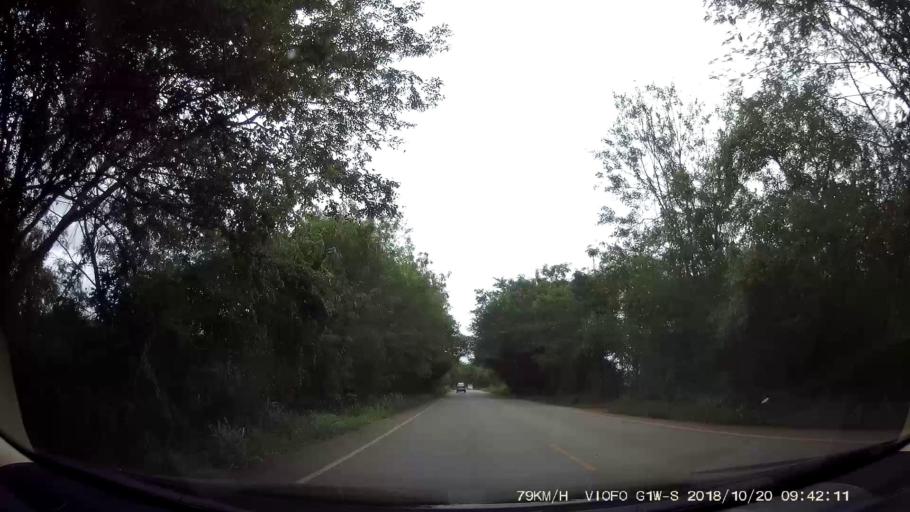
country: TH
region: Chaiyaphum
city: Khon San
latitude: 16.4612
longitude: 101.9535
